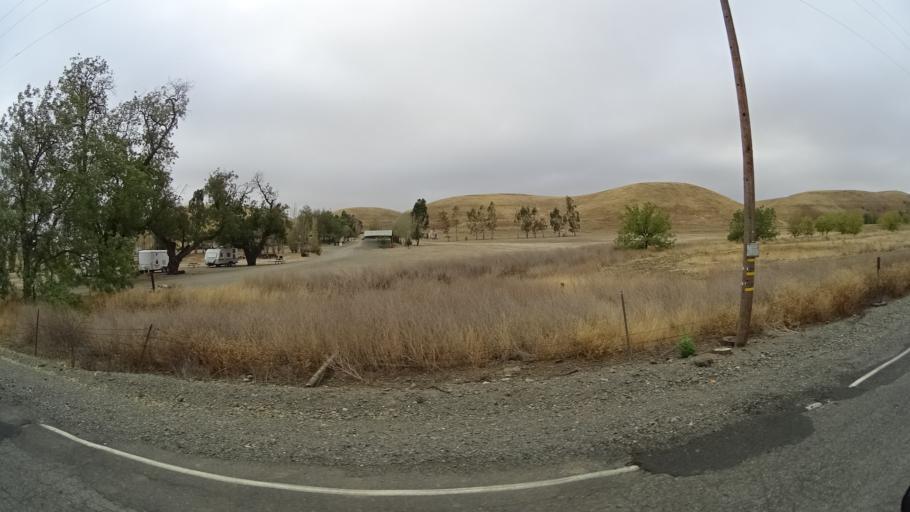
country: US
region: California
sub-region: Yolo County
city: Dunnigan
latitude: 38.8634
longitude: -122.0279
